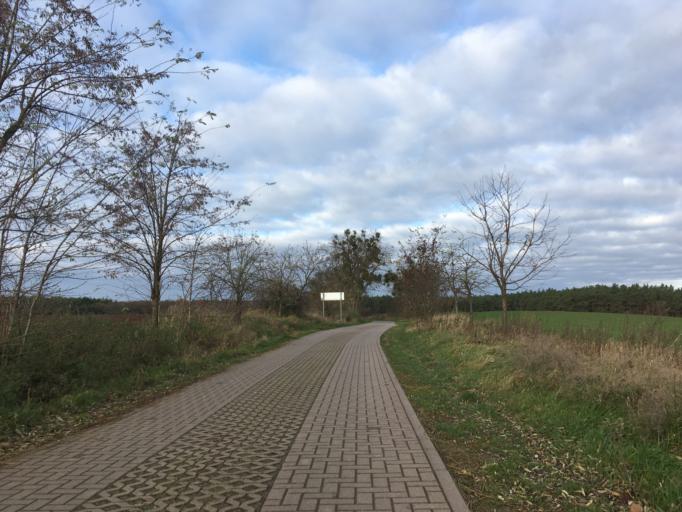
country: DE
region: Brandenburg
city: Muncheberg
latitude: 52.5597
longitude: 14.1356
